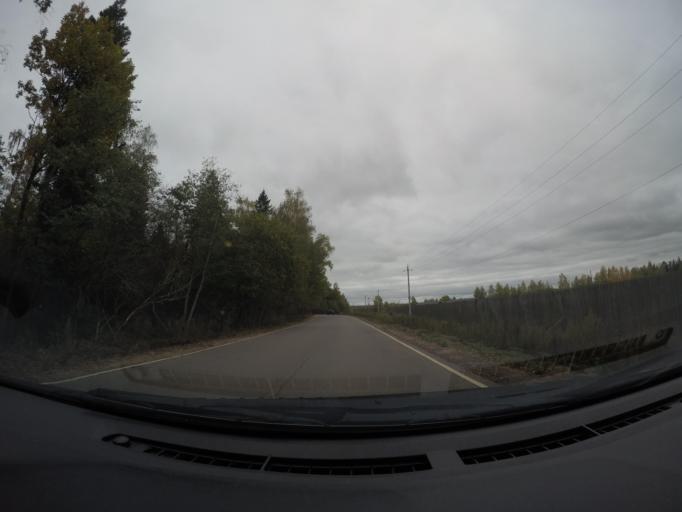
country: RU
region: Moskovskaya
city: Ruza
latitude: 55.7817
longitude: 36.2504
